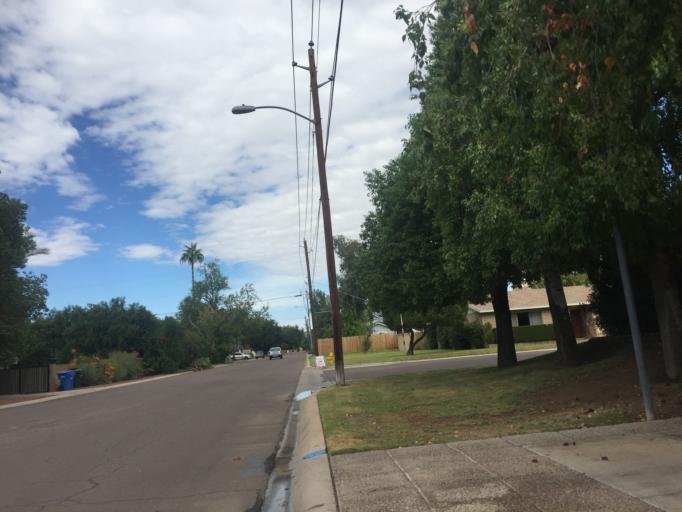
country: US
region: Arizona
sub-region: Maricopa County
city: Phoenix
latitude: 33.5331
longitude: -112.0693
